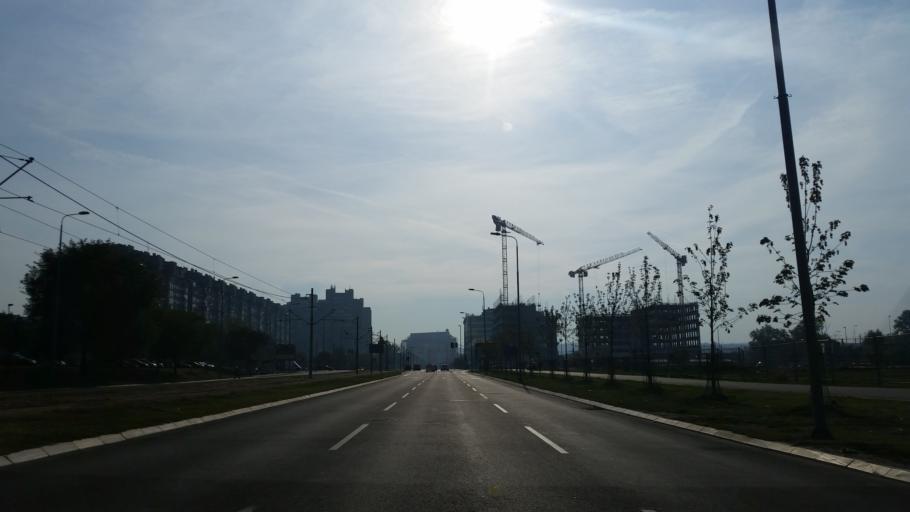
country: RS
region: Central Serbia
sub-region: Belgrade
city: Novi Beograd
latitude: 44.8092
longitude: 20.4173
